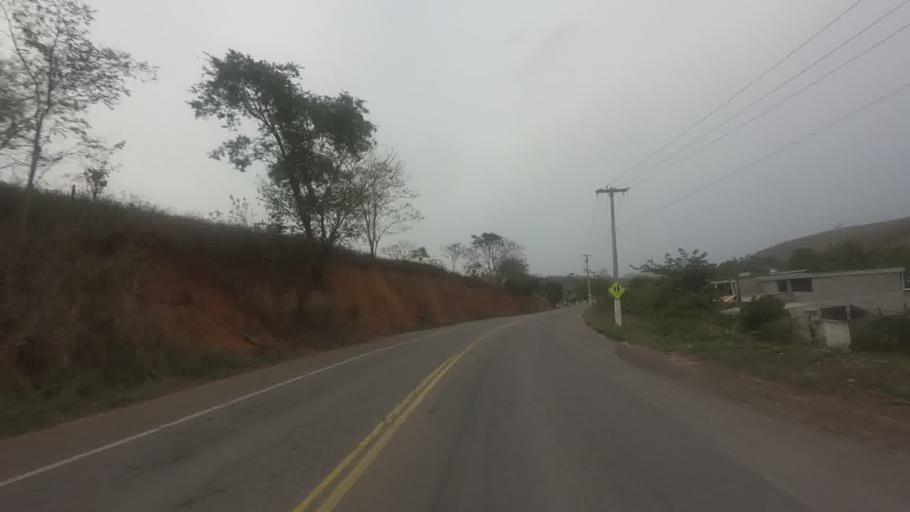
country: BR
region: Rio de Janeiro
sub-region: Santo Antonio De Padua
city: Santo Antonio de Padua
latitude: -21.6341
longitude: -42.2702
